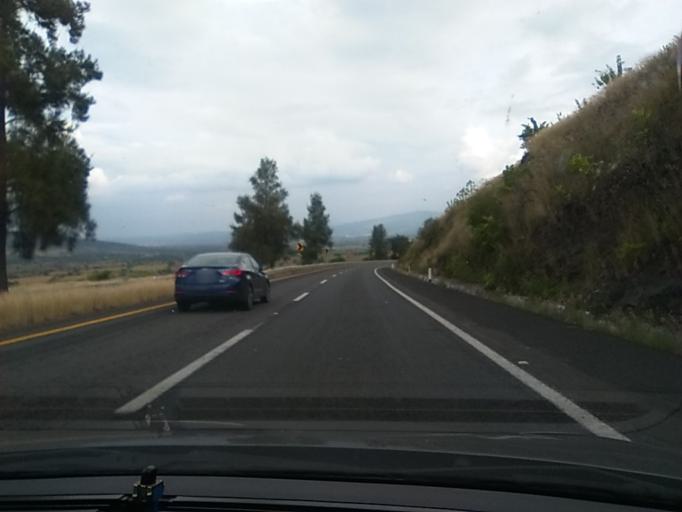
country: MX
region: Michoacan
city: Ixtlan
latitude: 20.1924
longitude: -102.3149
